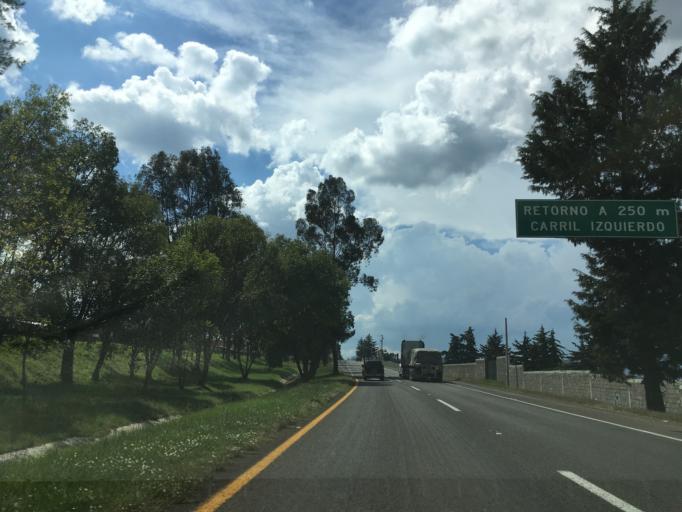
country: MX
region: Michoacan
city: Cuanajo
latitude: 19.5364
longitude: -101.5413
